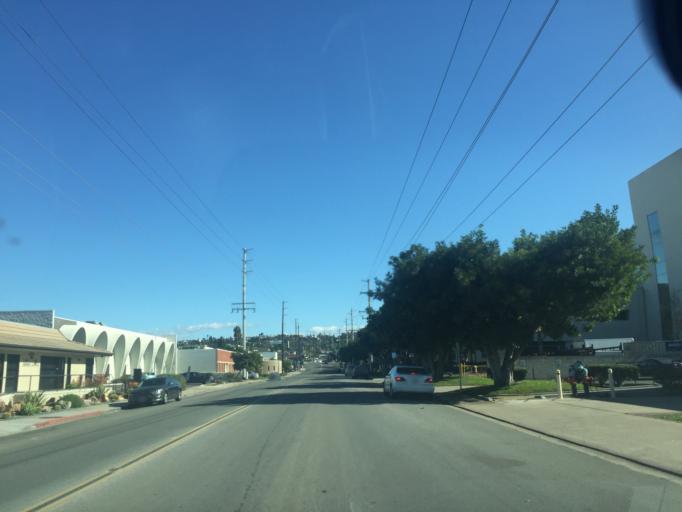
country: US
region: California
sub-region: San Diego County
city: La Mesa
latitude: 32.7877
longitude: -117.1012
